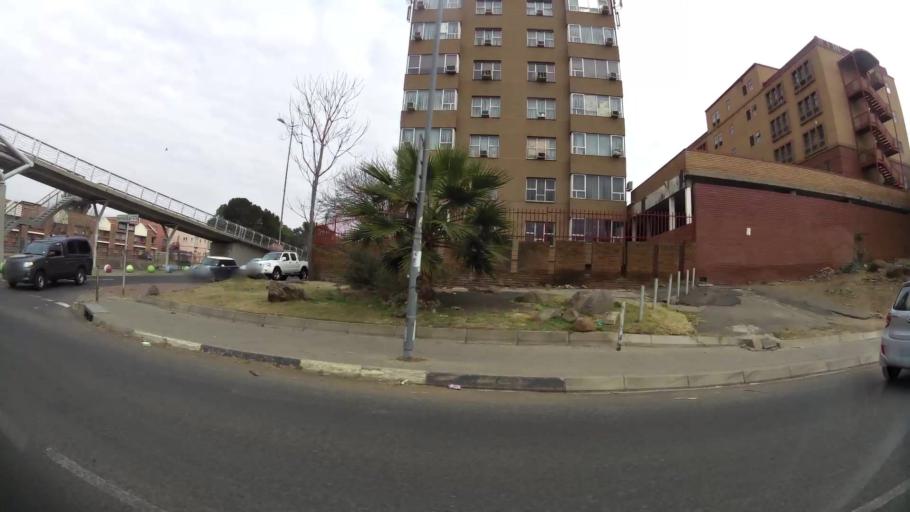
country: ZA
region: Orange Free State
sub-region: Mangaung Metropolitan Municipality
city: Bloemfontein
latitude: -29.1179
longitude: 26.2136
